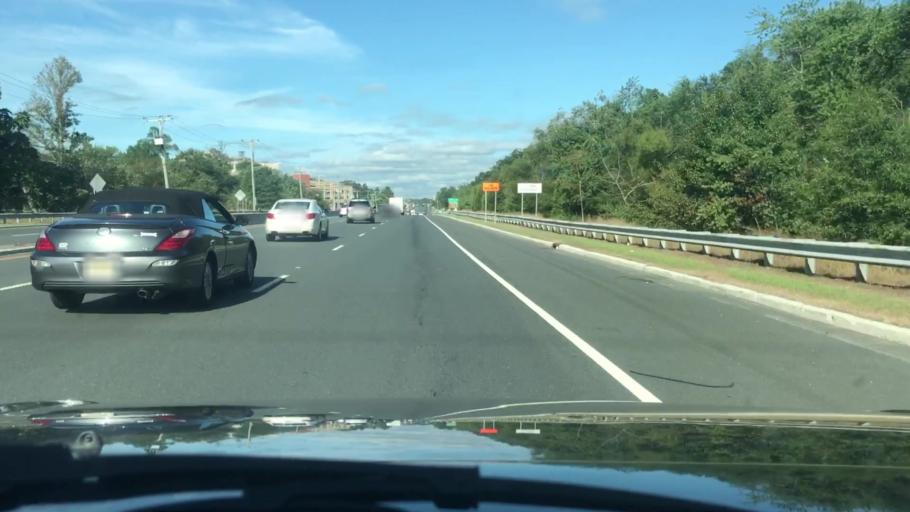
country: US
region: New Jersey
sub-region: Ocean County
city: Silver Ridge
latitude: 39.9646
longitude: -74.2108
